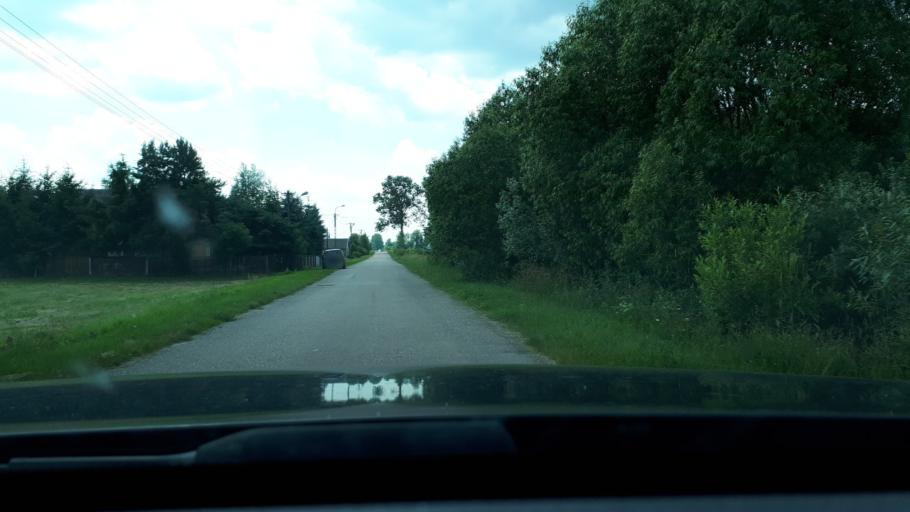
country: PL
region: Podlasie
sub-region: Powiat bialostocki
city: Lapy
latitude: 53.0891
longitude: 22.8418
